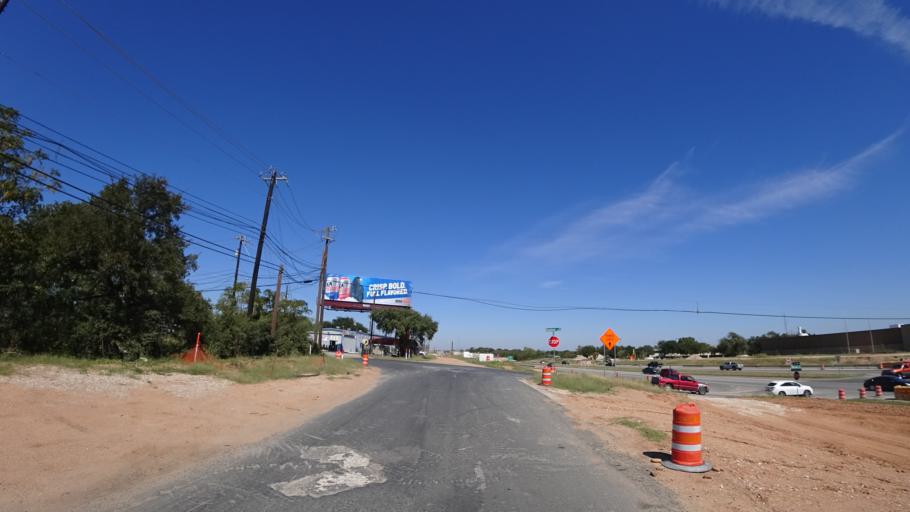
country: US
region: Texas
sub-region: Travis County
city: Austin
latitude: 30.2688
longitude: -97.6705
